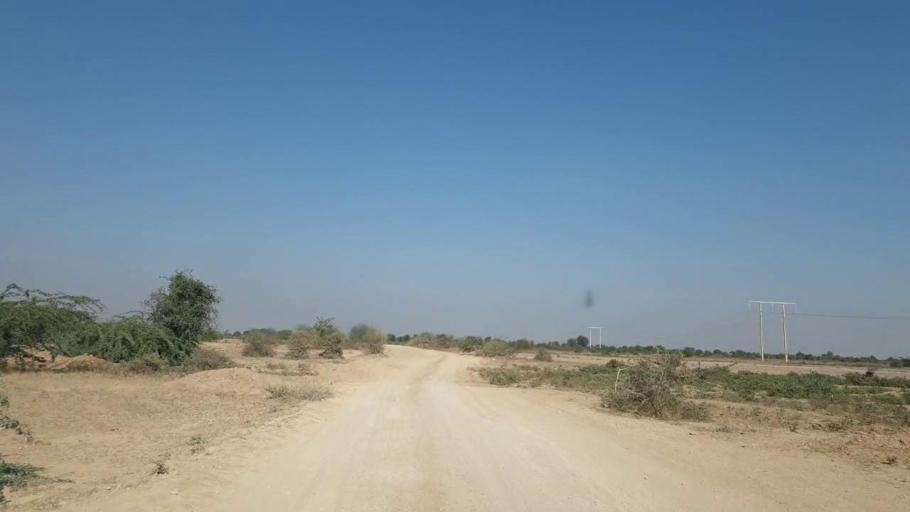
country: PK
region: Sindh
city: Jamshoro
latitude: 25.3132
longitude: 67.8190
